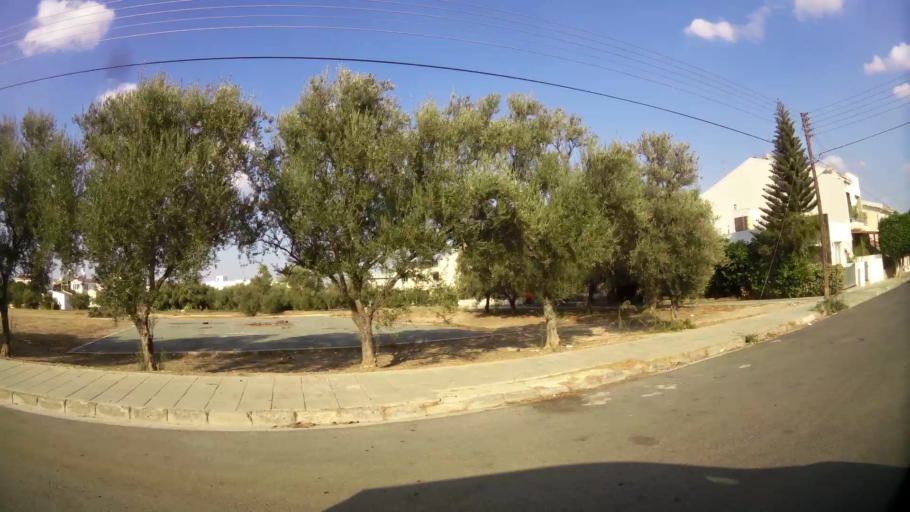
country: CY
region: Lefkosia
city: Kato Deftera
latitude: 35.1103
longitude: 33.2892
